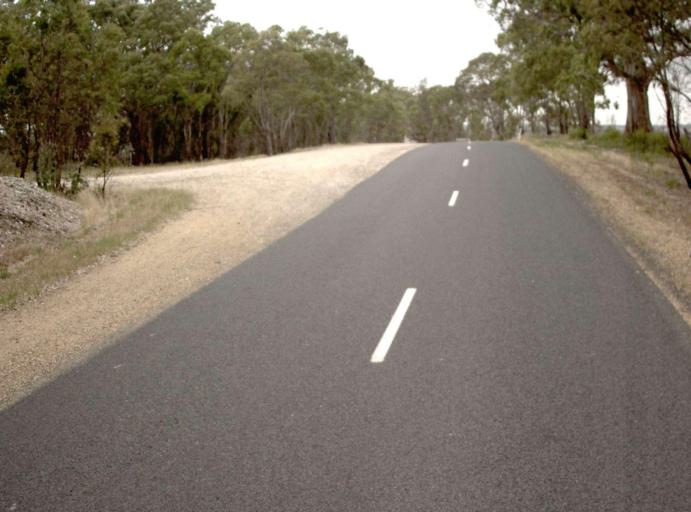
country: AU
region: Victoria
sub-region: Wellington
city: Heyfield
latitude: -37.8725
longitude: 146.7087
